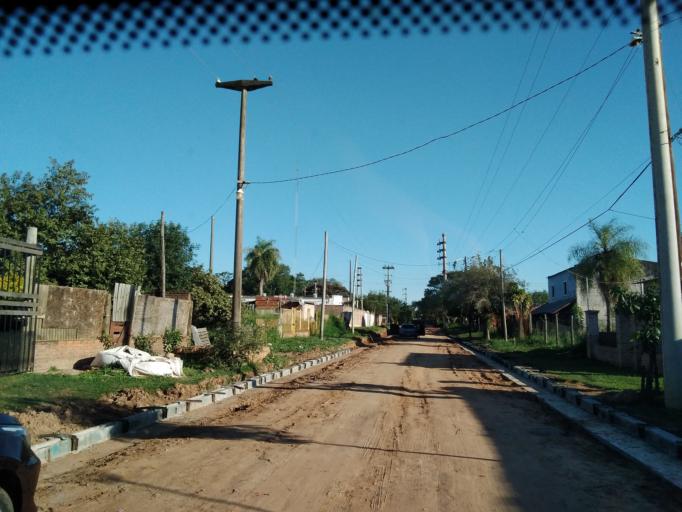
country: AR
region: Corrientes
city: Corrientes
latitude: -27.5050
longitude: -58.7943
